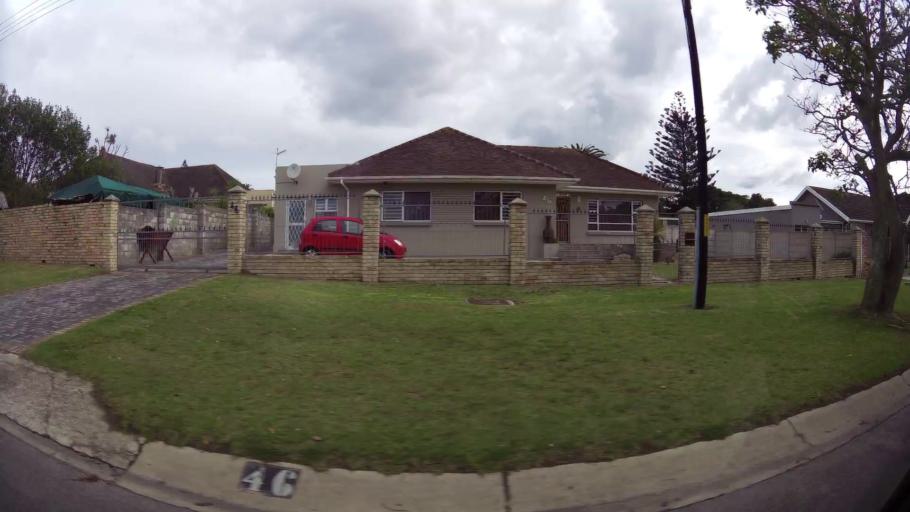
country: ZA
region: Eastern Cape
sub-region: Nelson Mandela Bay Metropolitan Municipality
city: Port Elizabeth
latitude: -33.9386
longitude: 25.5189
